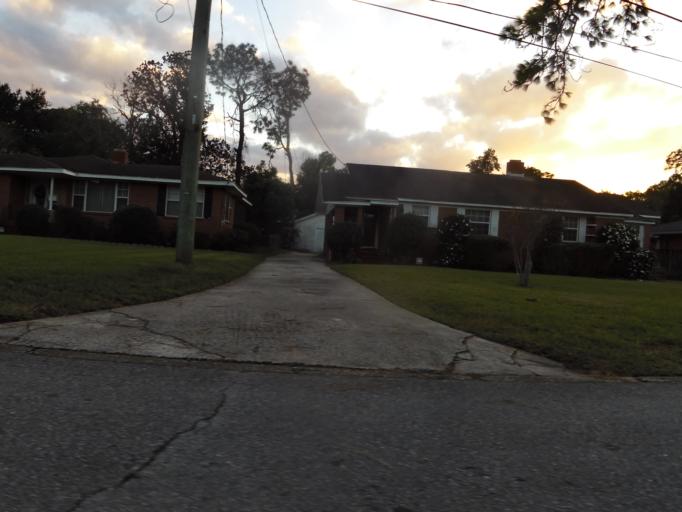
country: US
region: Florida
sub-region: Duval County
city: Jacksonville
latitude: 30.2817
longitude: -81.6563
